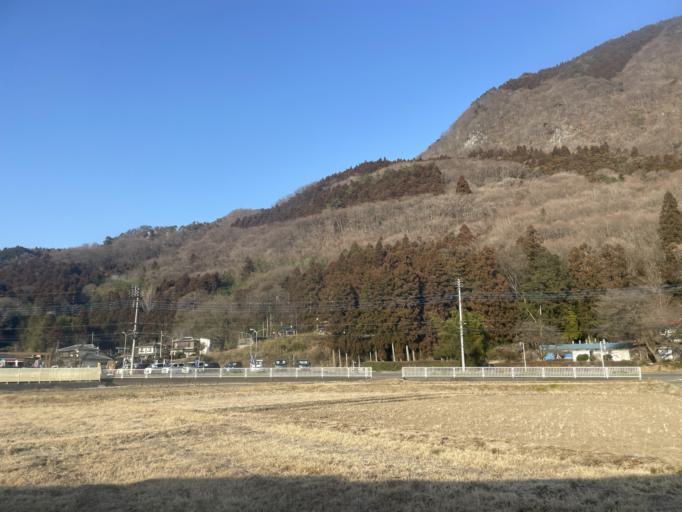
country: JP
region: Gunma
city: Nakanojomachi
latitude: 36.5781
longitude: 138.8732
